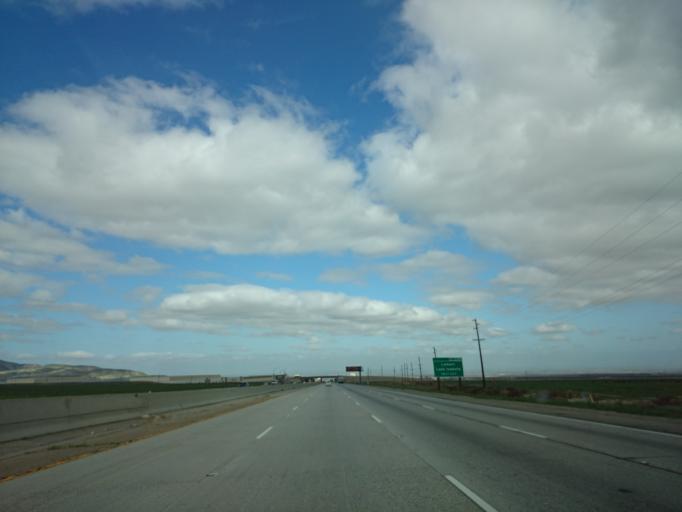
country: US
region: California
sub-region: Kern County
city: Frazier Park
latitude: 34.9656
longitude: -118.9386
